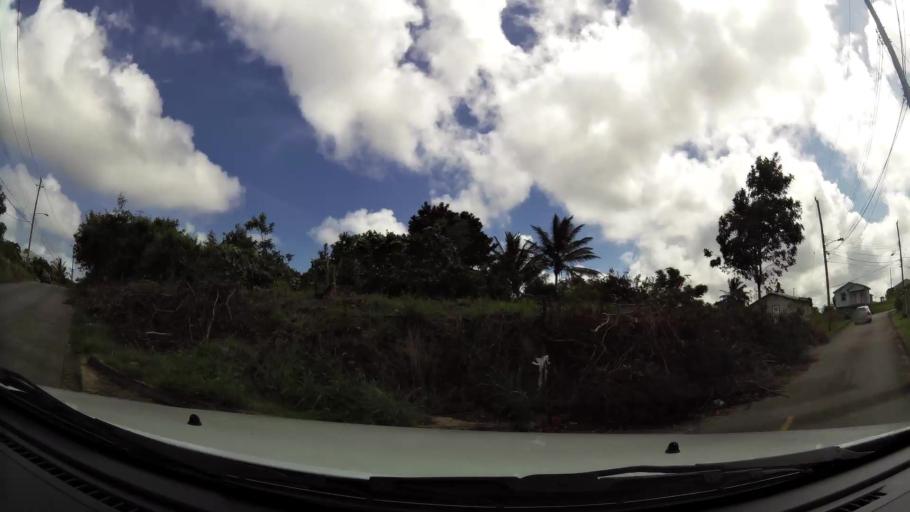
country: BB
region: Saint James
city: Holetown
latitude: 13.2071
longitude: -59.6016
